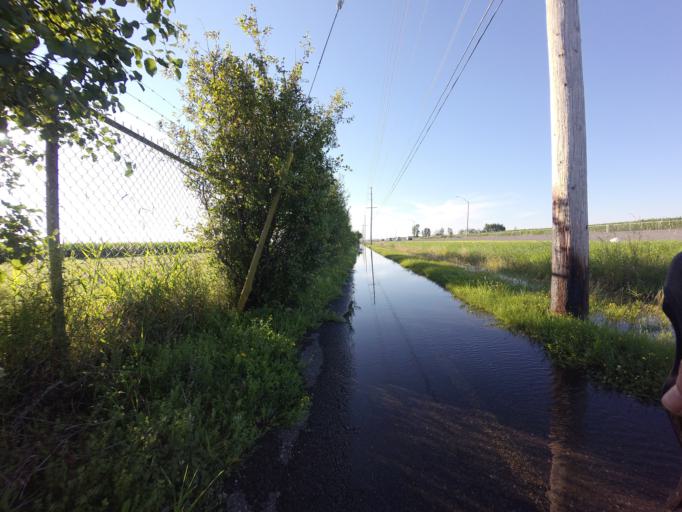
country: CA
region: Ontario
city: Bells Corners
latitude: 45.2980
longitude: -75.7631
